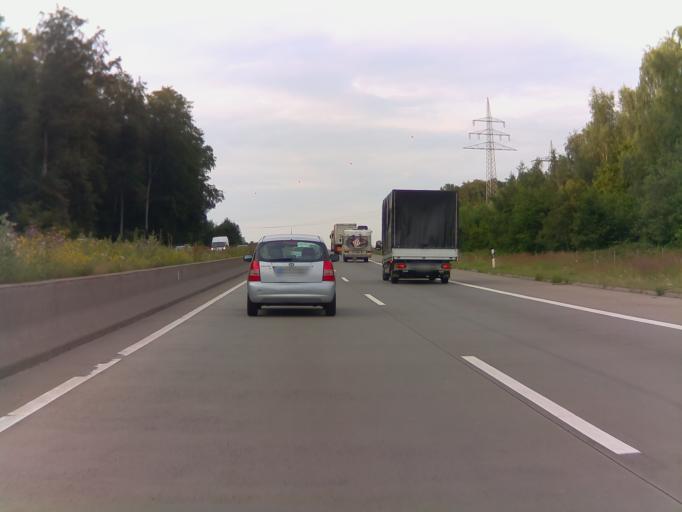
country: DE
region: Hesse
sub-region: Regierungsbezirk Giessen
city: Grossen Buseck
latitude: 50.5646
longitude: 8.7947
